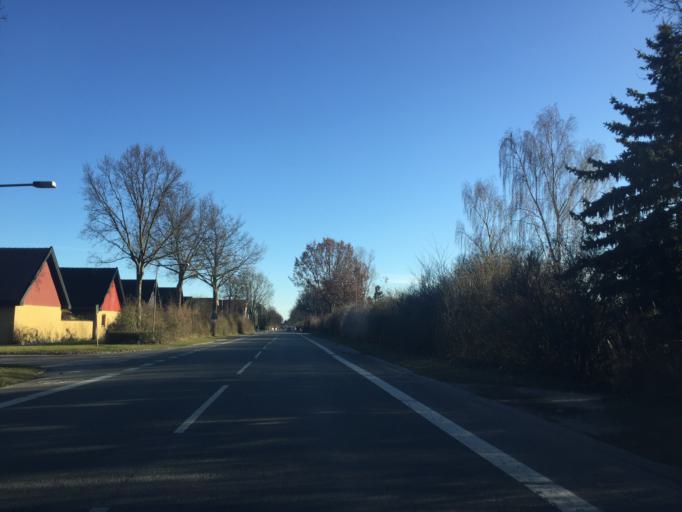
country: DK
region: Capital Region
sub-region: Dragor Kommune
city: Dragor
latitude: 55.5974
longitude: 12.6583
